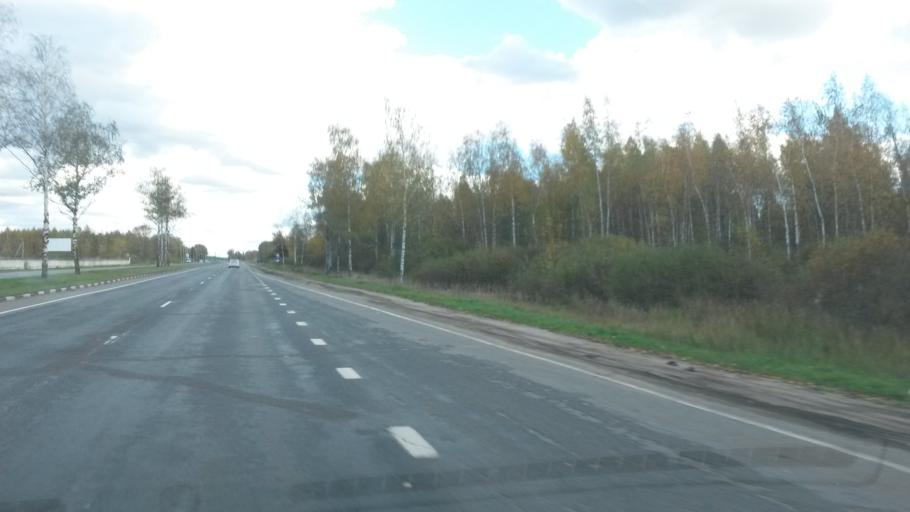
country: RU
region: Jaroslavl
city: Yaroslavl
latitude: 57.5407
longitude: 39.9810
